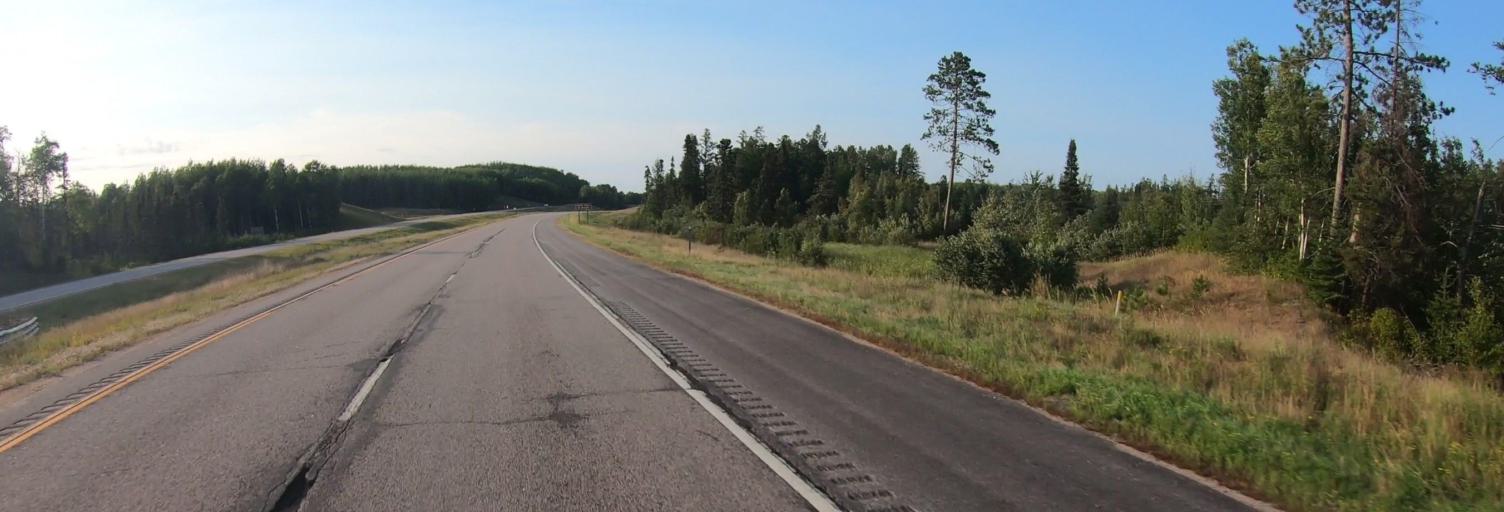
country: US
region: Minnesota
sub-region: Saint Louis County
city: Mountain Iron
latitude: 47.6785
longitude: -92.6361
